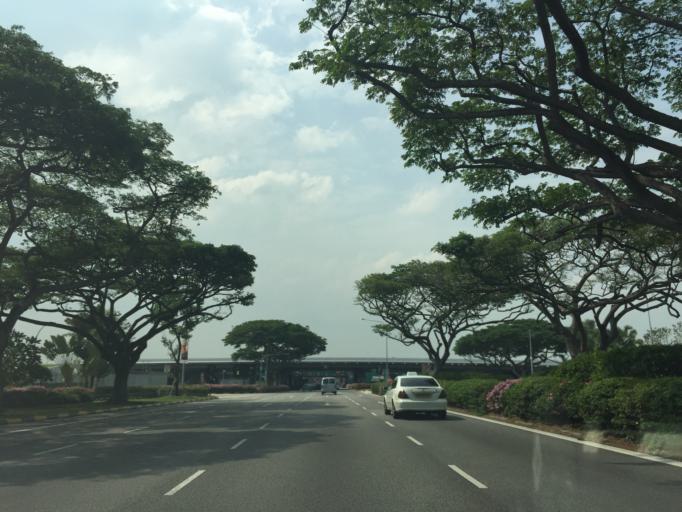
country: SG
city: Singapore
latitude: 1.3440
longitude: 103.9828
